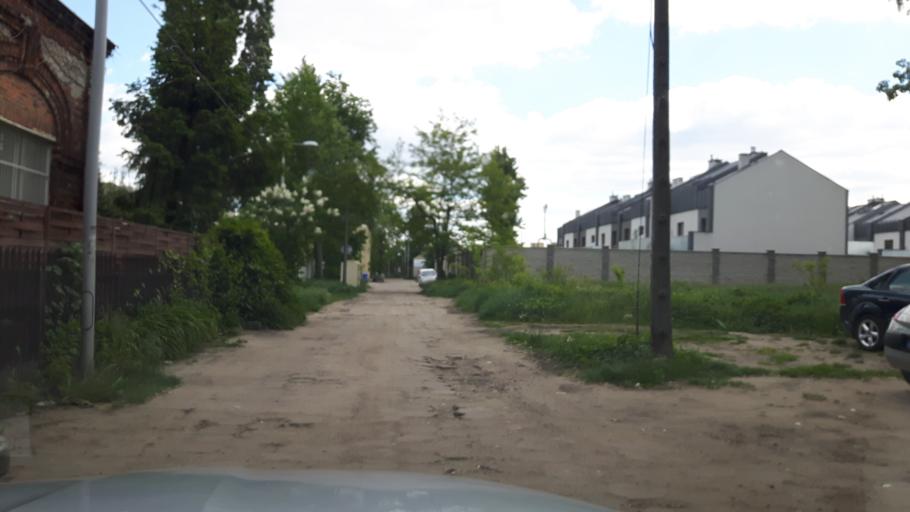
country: PL
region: Masovian Voivodeship
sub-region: Warszawa
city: Targowek
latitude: 52.2828
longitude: 21.0215
